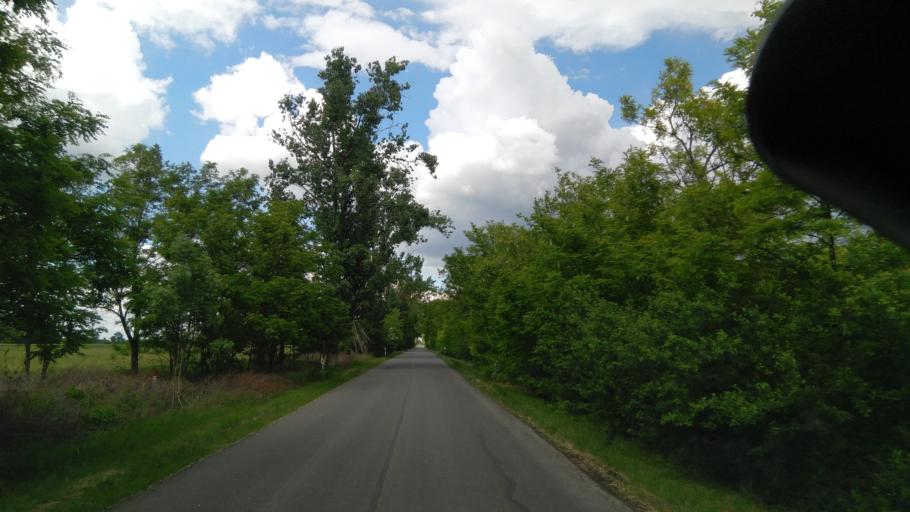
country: HU
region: Bekes
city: Bucsa
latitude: 47.1582
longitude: 21.0825
